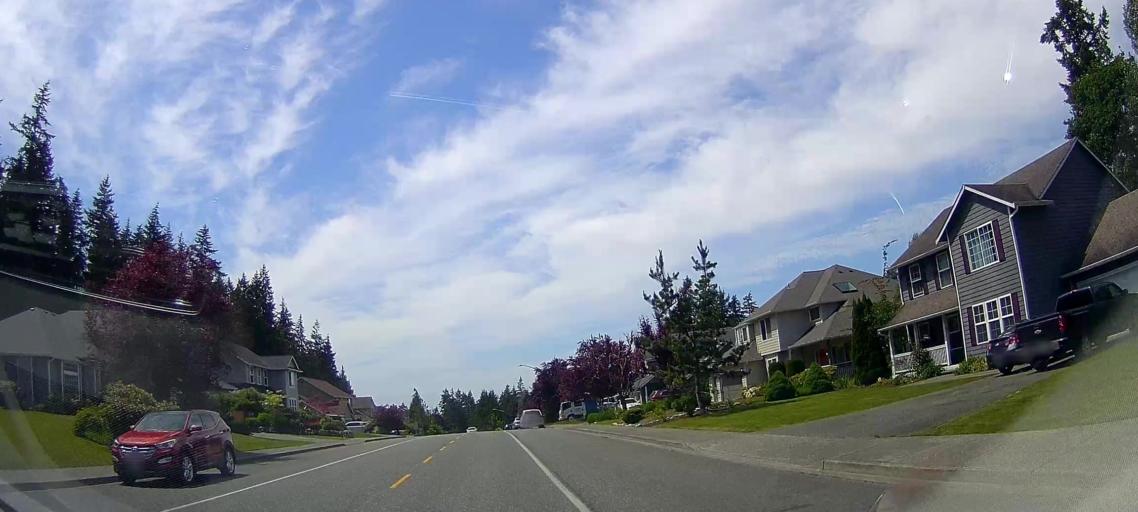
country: US
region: Washington
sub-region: Skagit County
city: Mount Vernon
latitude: 48.4160
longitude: -122.2928
